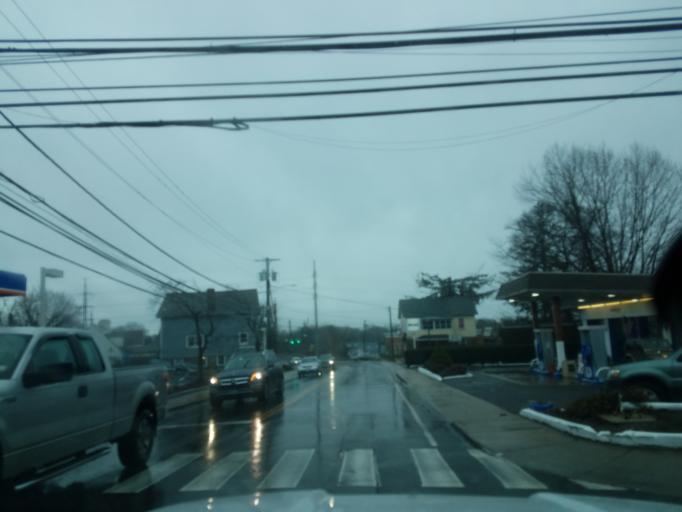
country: US
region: Connecticut
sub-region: Fairfield County
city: Darien
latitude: 41.0706
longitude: -73.4914
